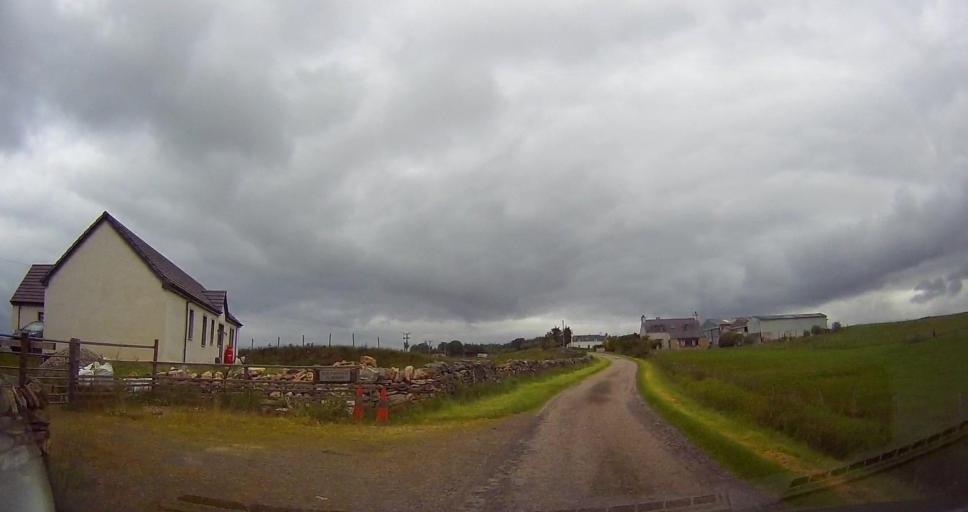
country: GB
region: Scotland
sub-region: Highland
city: Alness
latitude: 58.0771
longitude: -4.4439
